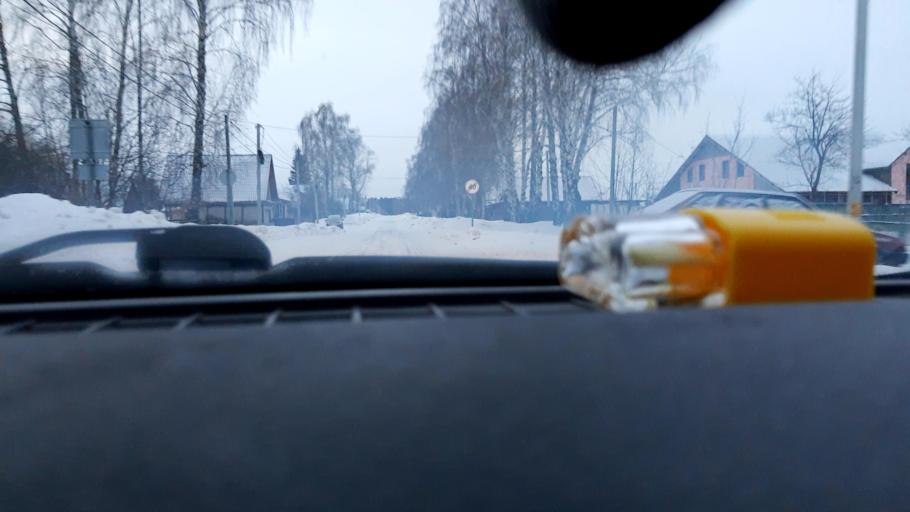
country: RU
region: Bashkortostan
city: Iglino
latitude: 54.8031
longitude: 56.4270
